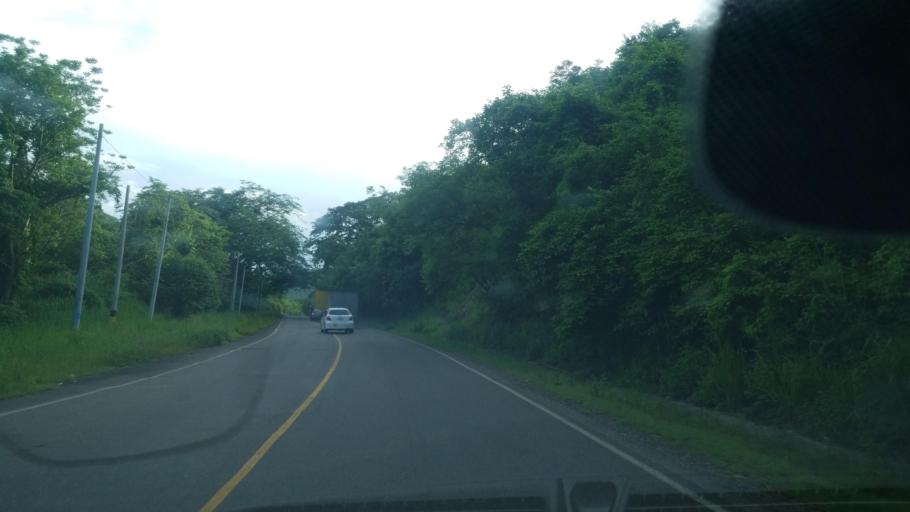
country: HN
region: Santa Barbara
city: Ilama
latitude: 15.0881
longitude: -88.2138
